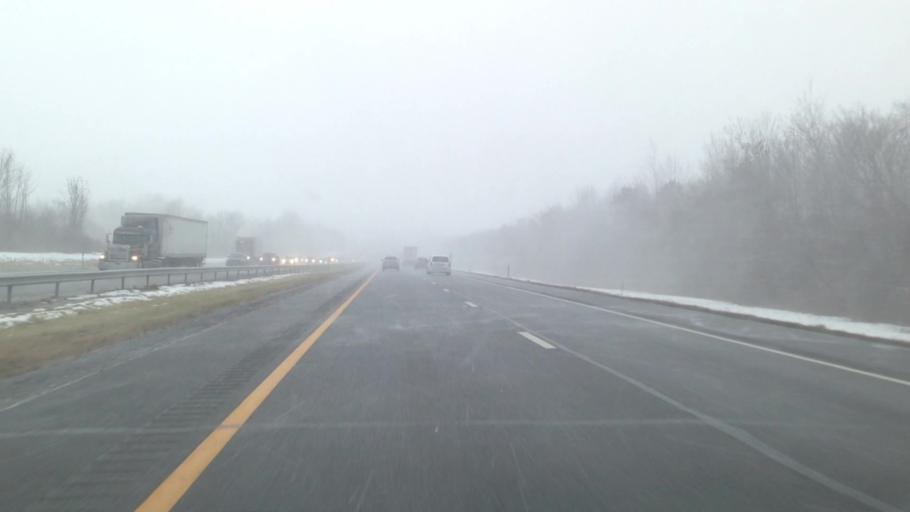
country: US
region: New York
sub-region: Montgomery County
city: Hagaman
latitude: 42.8999
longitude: -74.1105
